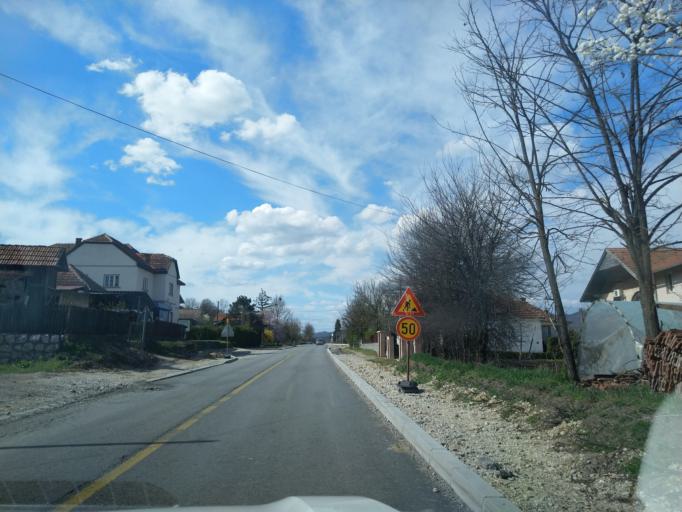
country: RS
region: Central Serbia
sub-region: Zlatiborski Okrug
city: Pozega
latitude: 43.8274
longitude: 20.0777
